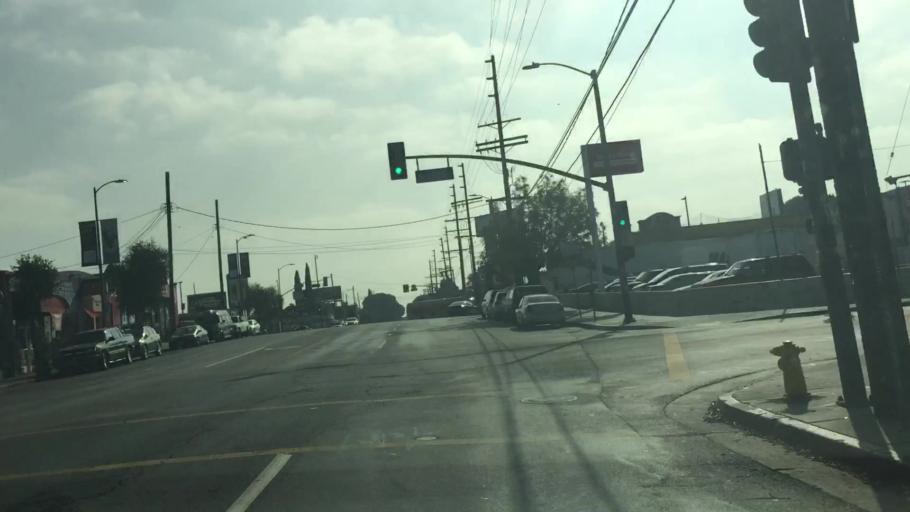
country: US
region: California
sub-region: Los Angeles County
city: Boyle Heights
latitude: 34.0412
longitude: -118.2132
